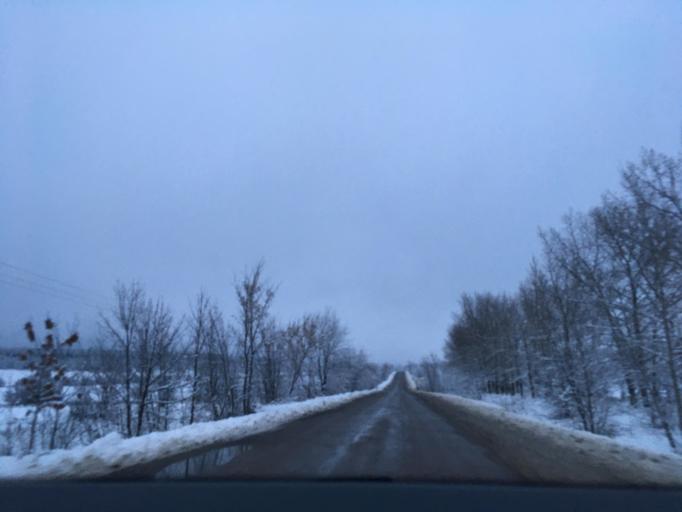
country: RU
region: Voronezj
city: Verkhniy Mamon
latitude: 50.0613
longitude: 40.2680
